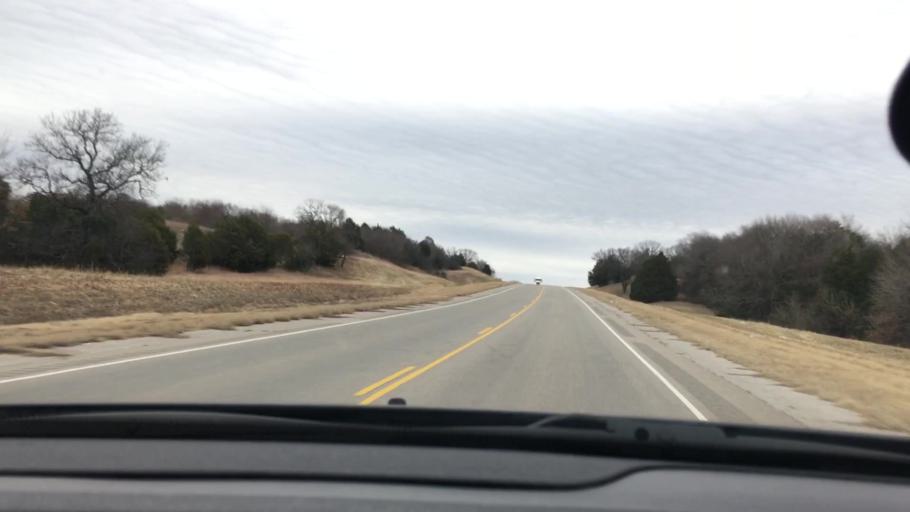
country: US
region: Oklahoma
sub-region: Johnston County
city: Tishomingo
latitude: 34.2358
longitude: -96.7797
